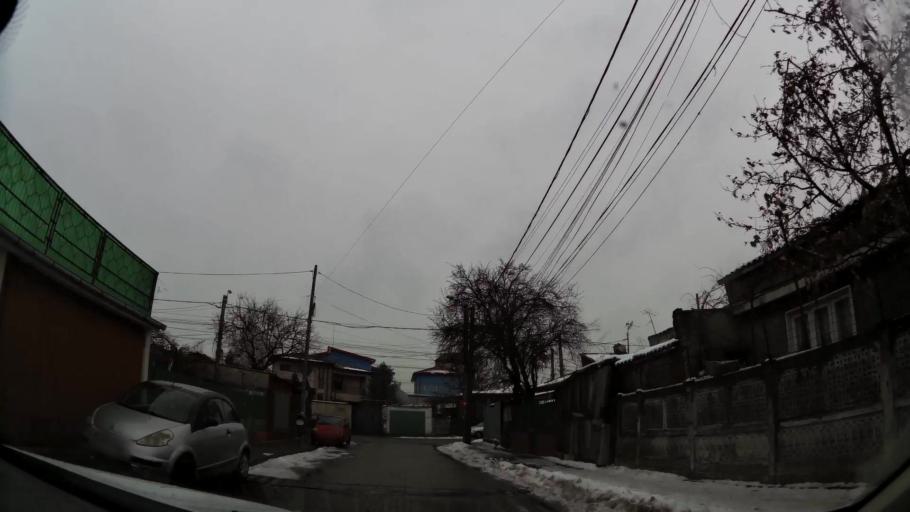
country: RO
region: Ilfov
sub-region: Comuna Mogosoaia
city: Mogosoaia
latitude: 44.4942
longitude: 26.0283
